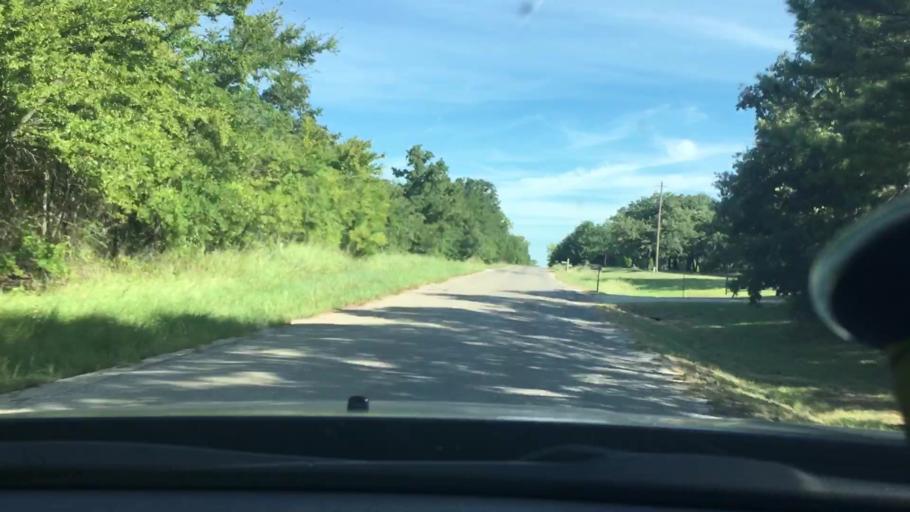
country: US
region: Oklahoma
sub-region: Carter County
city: Lone Grove
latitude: 34.2486
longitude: -97.2475
